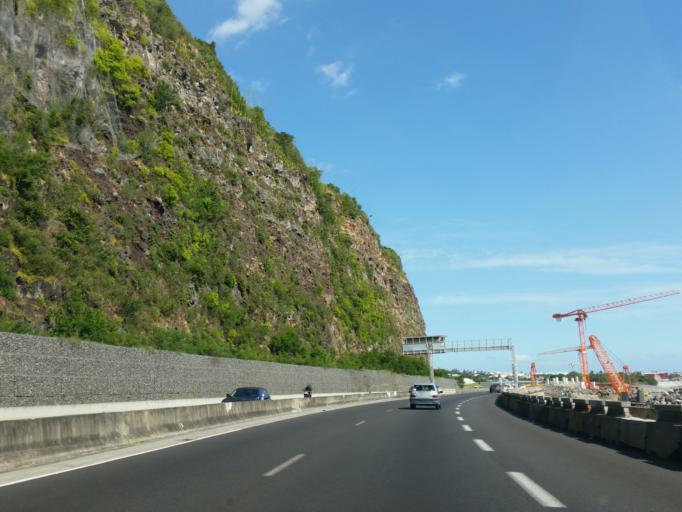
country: RE
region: Reunion
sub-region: Reunion
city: La Possession
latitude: -20.9185
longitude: 55.3487
